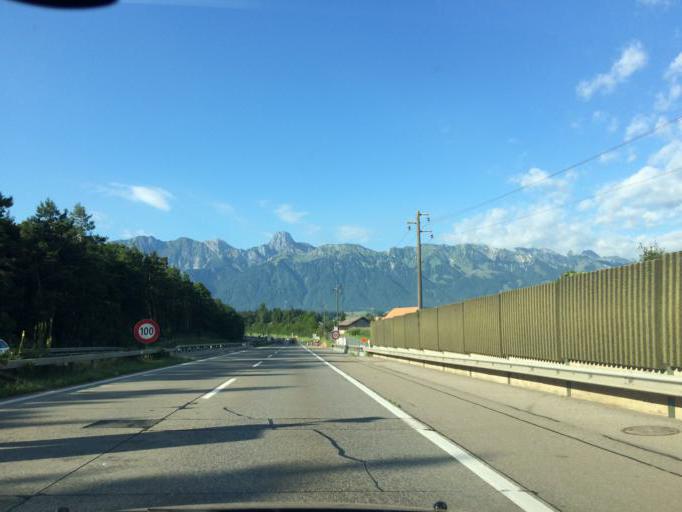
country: CH
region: Bern
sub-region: Thun District
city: Heimberg
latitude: 46.7707
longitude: 7.5976
